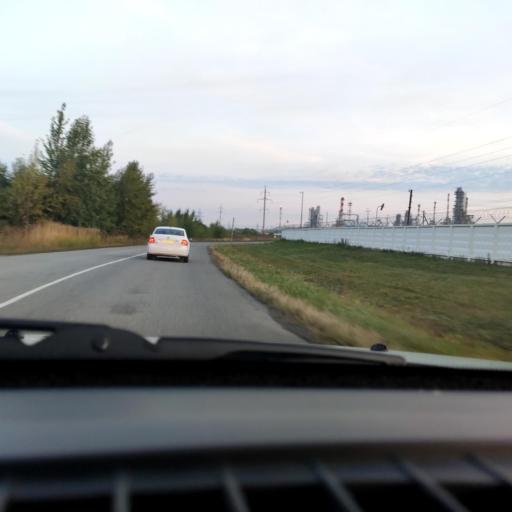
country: RU
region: Perm
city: Gamovo
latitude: 57.9027
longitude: 56.1275
